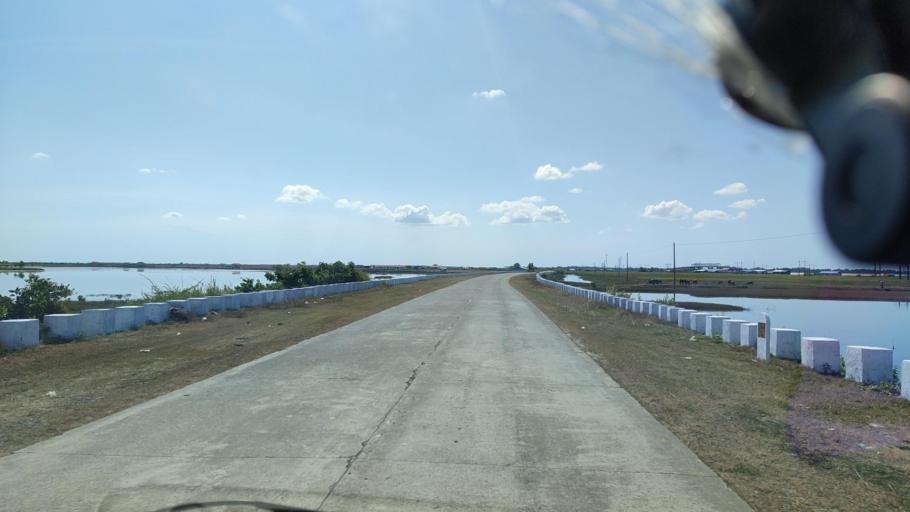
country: MM
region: Rakhine
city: Sittwe
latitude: 20.3079
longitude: 92.9088
